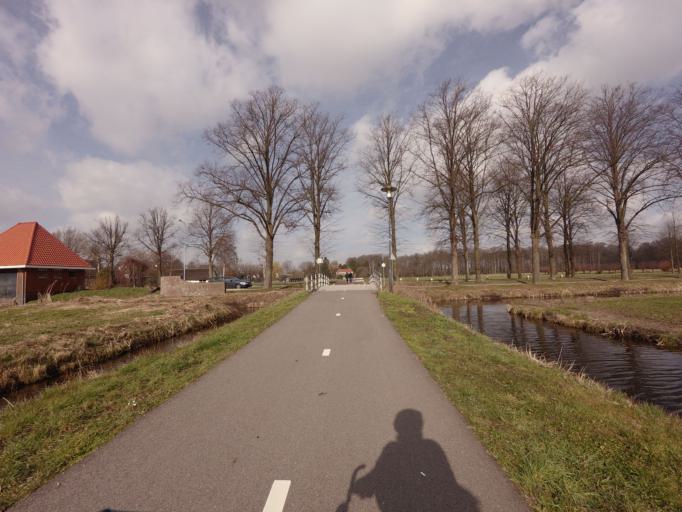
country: NL
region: North Holland
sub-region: Gemeente Wijdemeren
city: Kortenhoef
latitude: 52.2379
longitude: 5.1229
